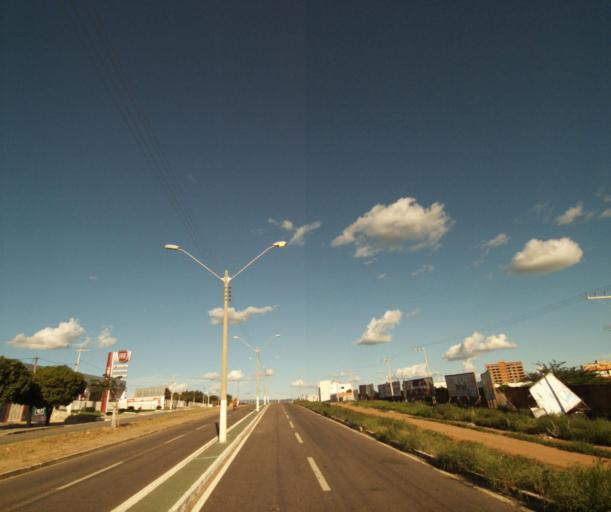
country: BR
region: Bahia
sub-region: Guanambi
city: Guanambi
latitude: -14.2093
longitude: -42.7707
